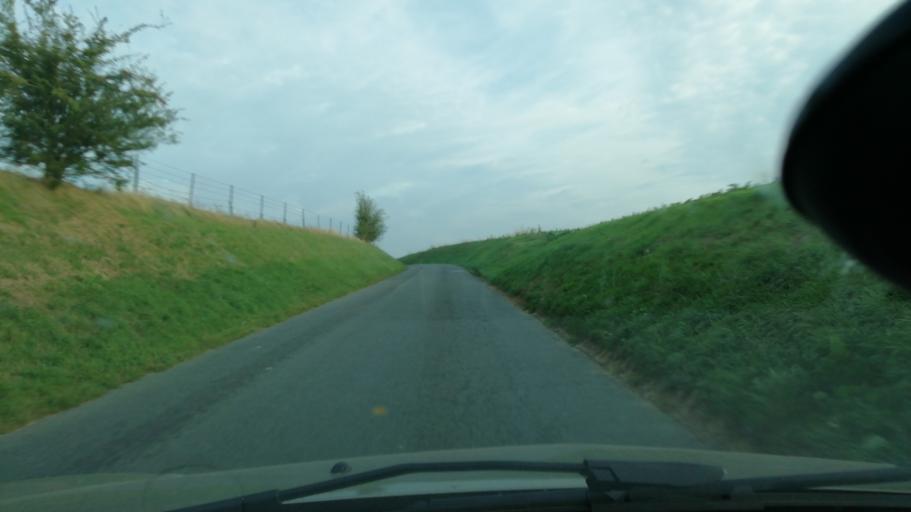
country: FR
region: Nord-Pas-de-Calais
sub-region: Departement du Nord
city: Viesly
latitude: 50.1174
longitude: 3.4680
